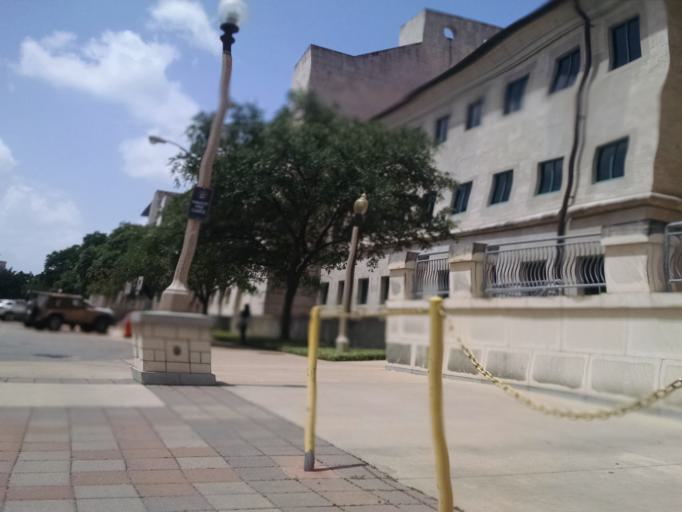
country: US
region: Texas
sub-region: Travis County
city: Austin
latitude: 30.2893
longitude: -97.7368
